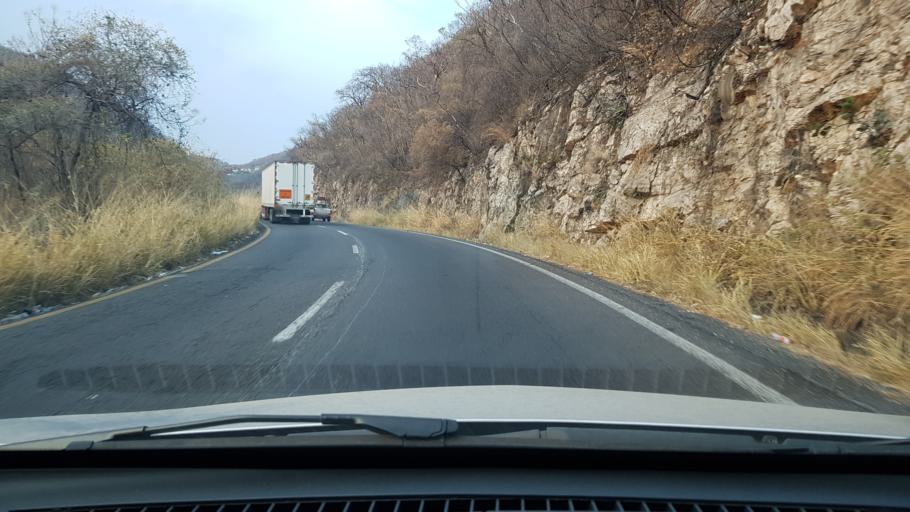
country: MX
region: Morelos
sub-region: Jiutepec
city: Independencia
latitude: 18.8633
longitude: -99.1215
